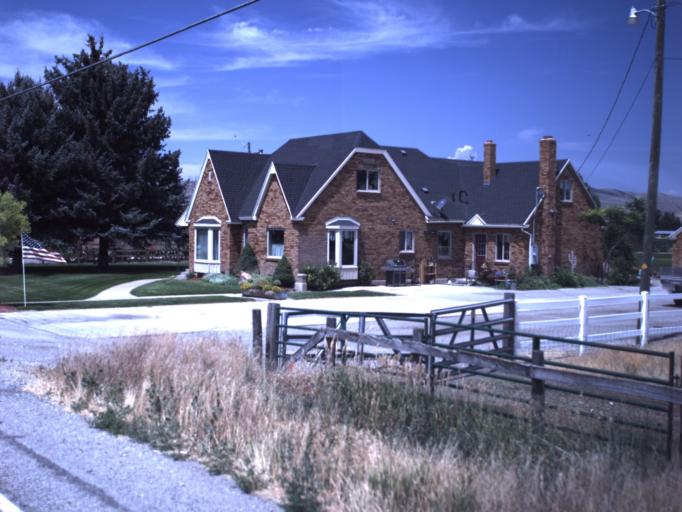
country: US
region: Utah
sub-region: Box Elder County
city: Elwood
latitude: 41.7124
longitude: -112.1380
